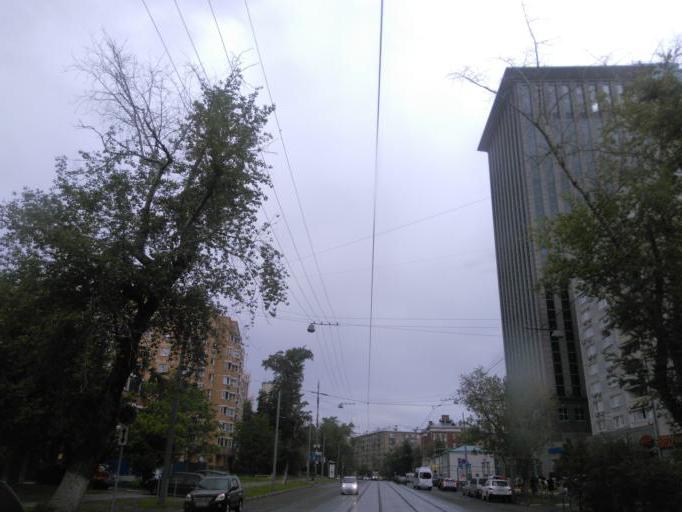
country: RU
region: Moscow
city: Zamoskvorech'ye
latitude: 55.7241
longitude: 37.6365
